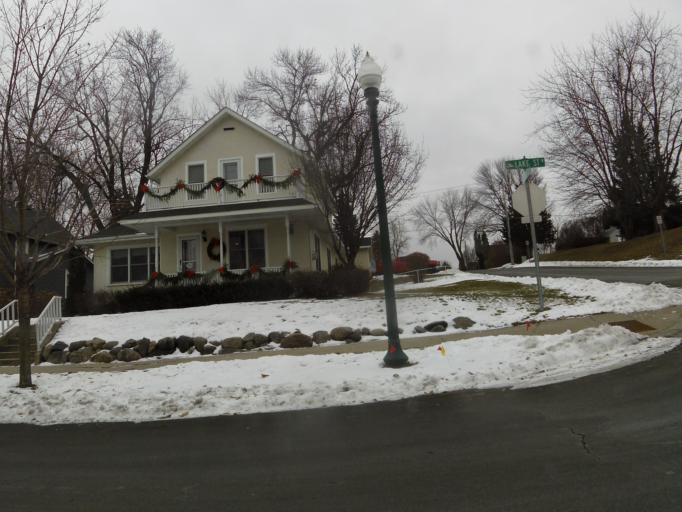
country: US
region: Minnesota
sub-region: Carver County
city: Waconia
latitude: 44.8516
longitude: -93.7921
